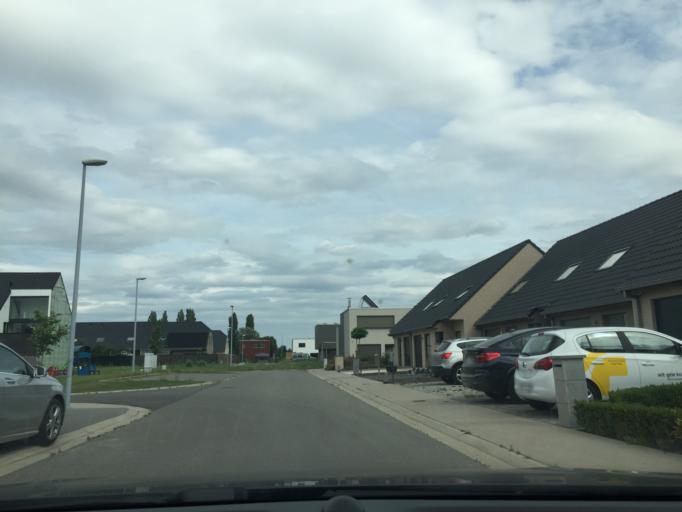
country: BE
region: Flanders
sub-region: Provincie West-Vlaanderen
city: Izegem
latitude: 50.9090
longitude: 3.2278
